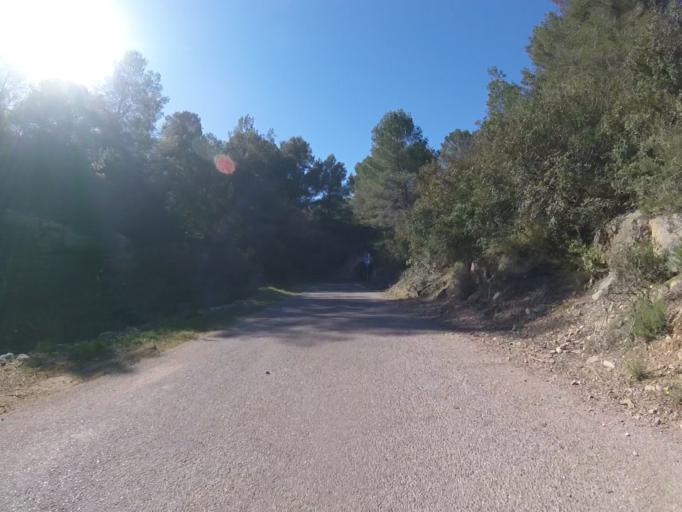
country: ES
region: Valencia
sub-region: Provincia de Castello
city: Orpesa/Oropesa del Mar
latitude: 40.0803
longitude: 0.1191
